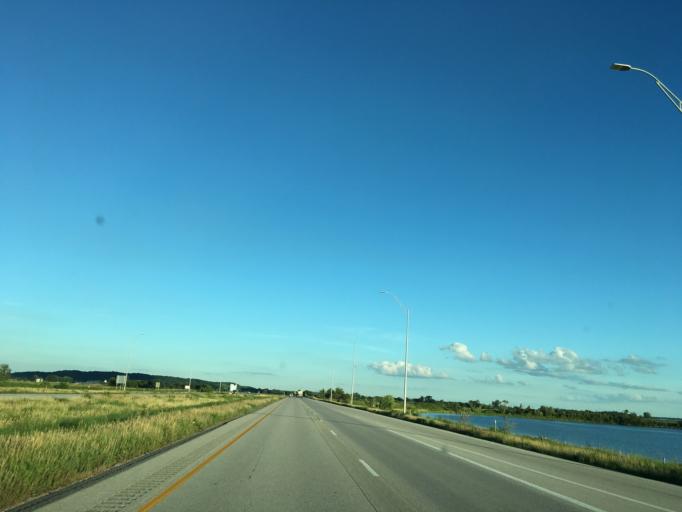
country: US
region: Iowa
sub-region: Fremont County
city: Hamburg
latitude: 40.5983
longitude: -95.6757
